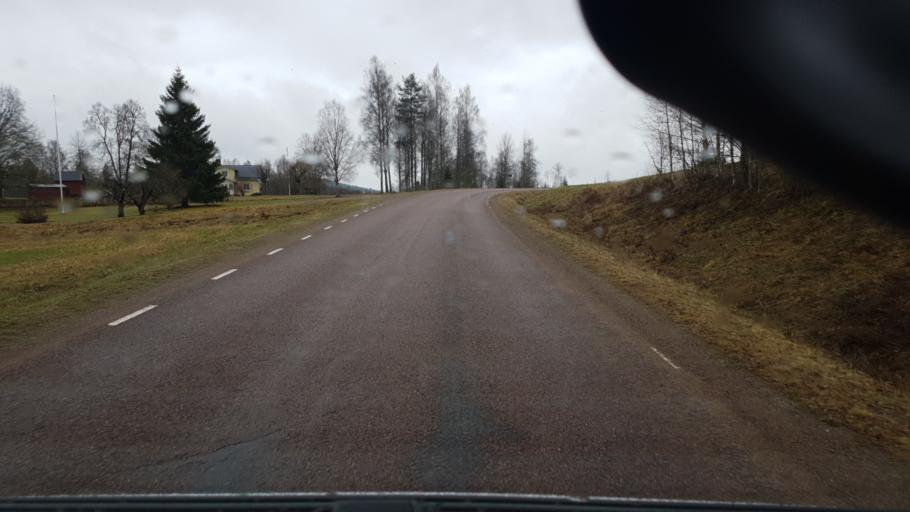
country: SE
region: Vaermland
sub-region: Eda Kommun
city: Charlottenberg
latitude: 59.9590
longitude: 12.3957
